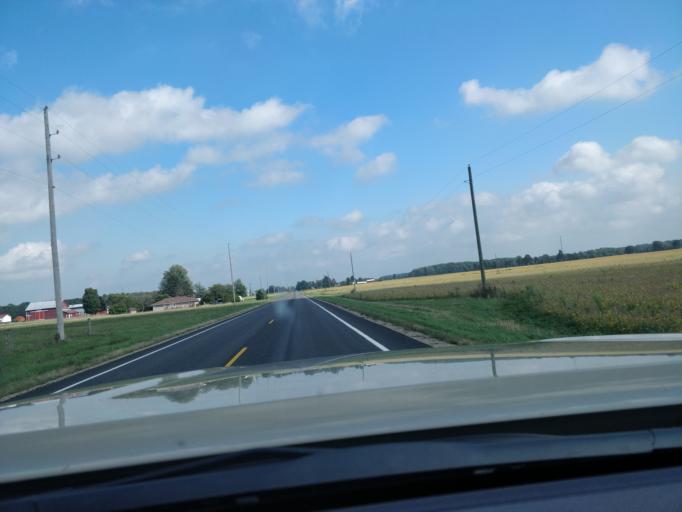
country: US
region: Michigan
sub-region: Ionia County
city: Lake Odessa
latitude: 42.8861
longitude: -85.1177
